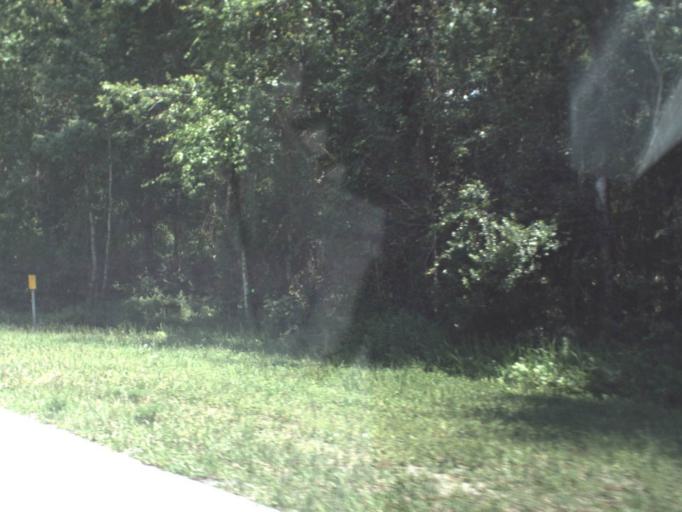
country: US
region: Florida
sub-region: Saint Johns County
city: Saint Augustine Shores
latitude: 29.7261
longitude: -81.4243
